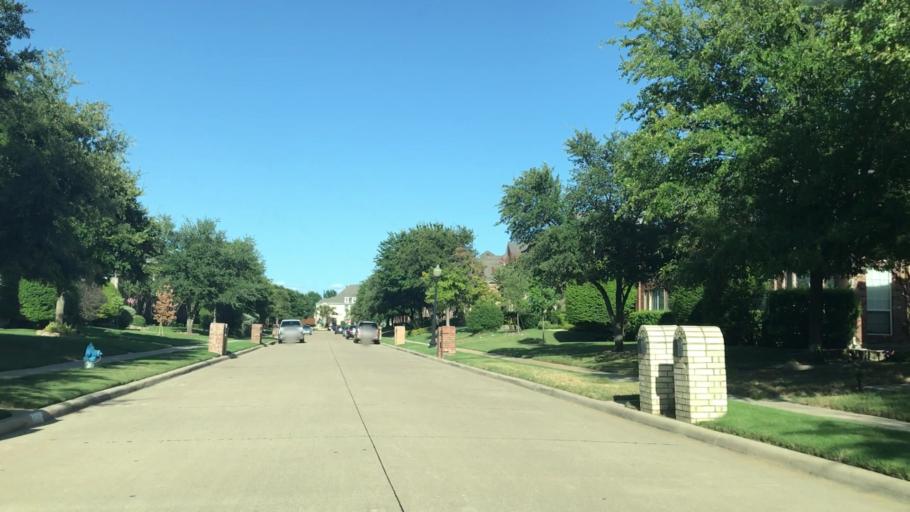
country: US
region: Texas
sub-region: Collin County
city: Frisco
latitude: 33.1360
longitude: -96.7807
